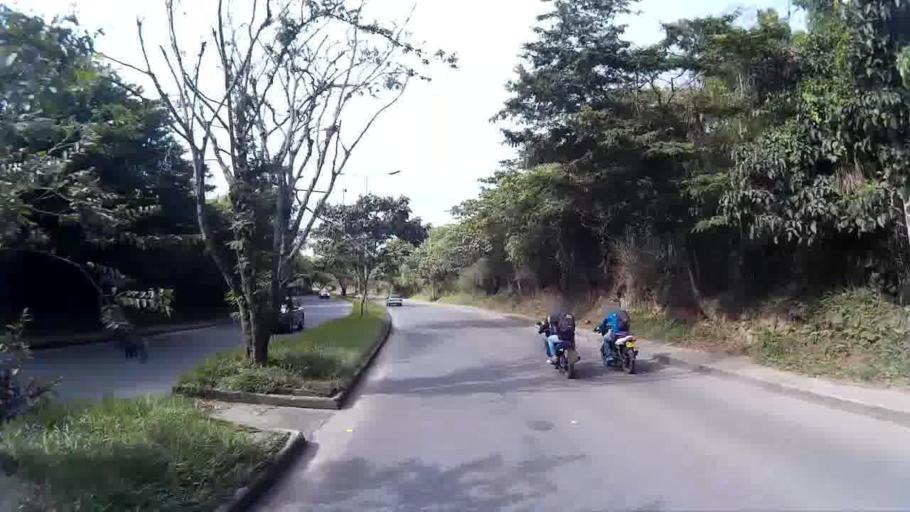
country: CO
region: Quindio
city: Calarca
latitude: 4.5484
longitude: -75.6547
